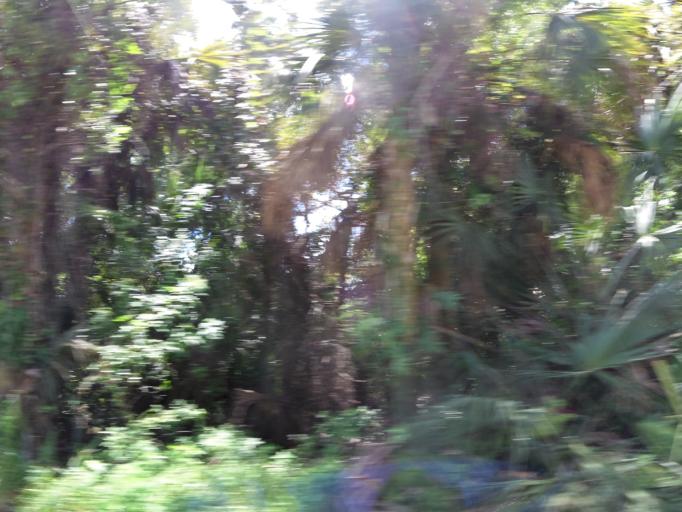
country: US
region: Florida
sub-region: Brevard County
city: Mims
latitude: 28.6372
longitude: -80.8444
